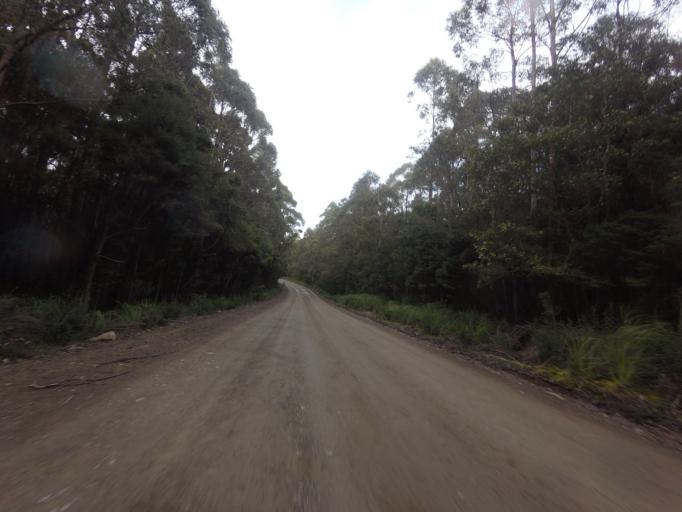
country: AU
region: Tasmania
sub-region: Huon Valley
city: Geeveston
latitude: -43.5175
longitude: 146.8850
